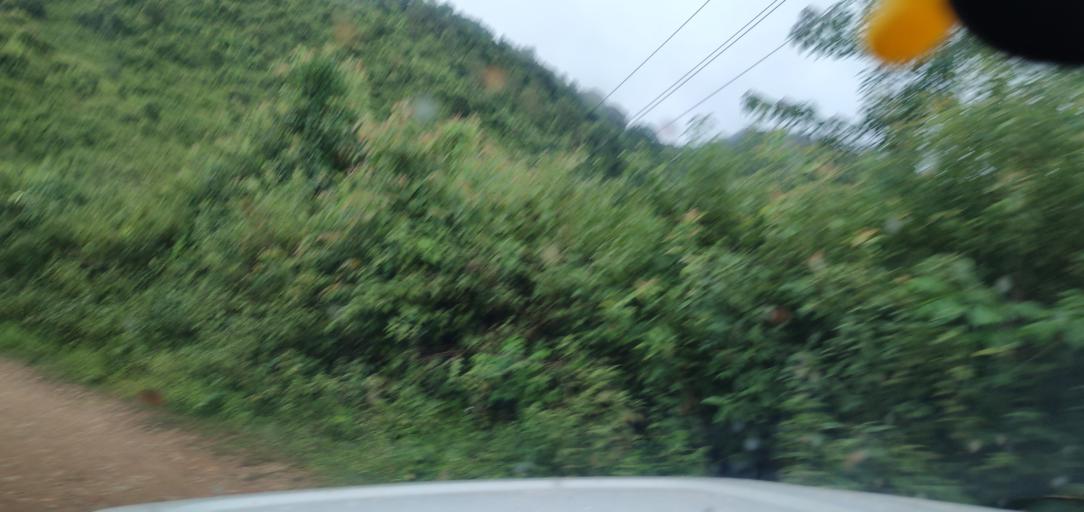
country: LA
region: Phongsali
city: Phongsali
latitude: 21.4470
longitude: 102.2887
